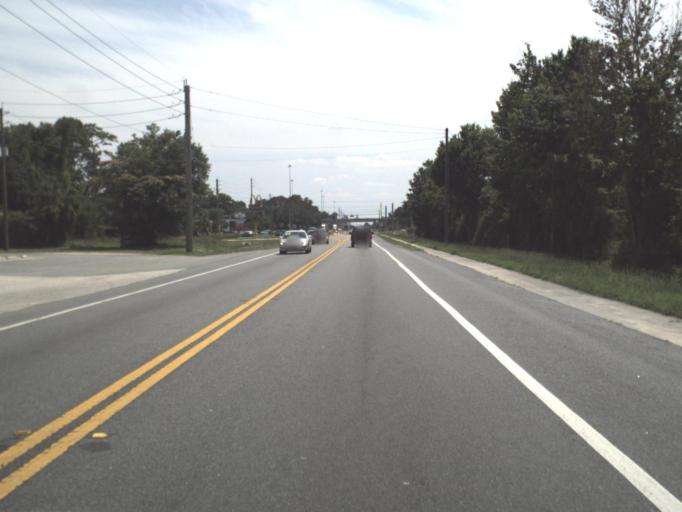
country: US
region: Florida
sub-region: Duval County
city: Jacksonville
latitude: 30.4648
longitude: -81.6335
